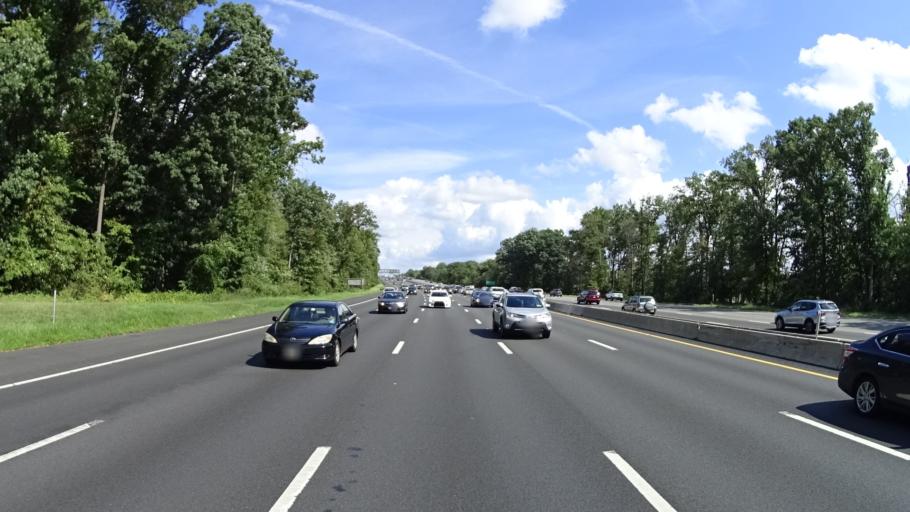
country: US
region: New Jersey
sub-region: Union County
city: Winfield
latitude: 40.6460
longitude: -74.2877
